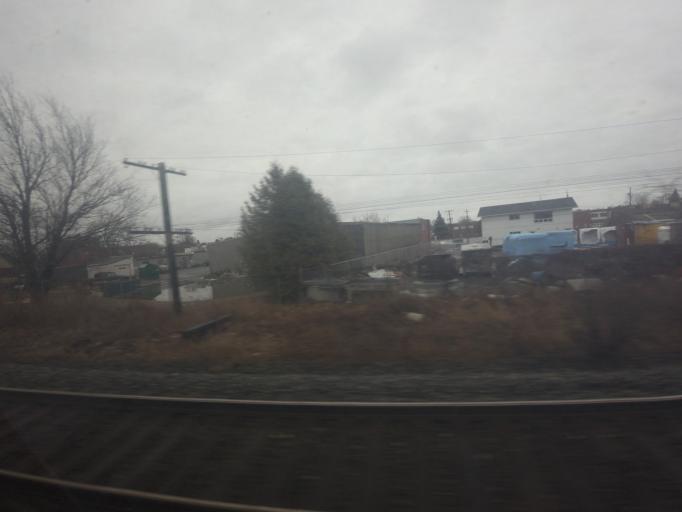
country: CA
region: Ontario
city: Kingston
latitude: 44.2386
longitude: -76.5765
